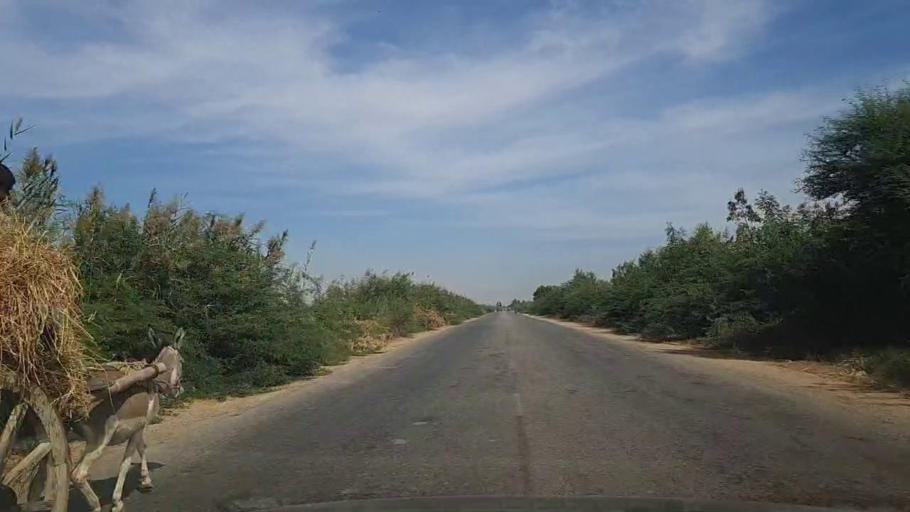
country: PK
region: Sindh
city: Daro Mehar
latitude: 24.9755
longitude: 68.1274
